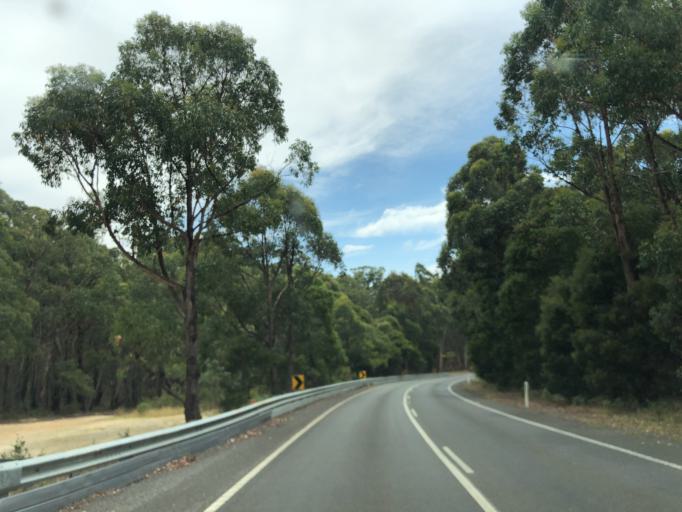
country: AU
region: Victoria
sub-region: Moorabool
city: Bacchus Marsh
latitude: -37.4891
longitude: 144.3040
